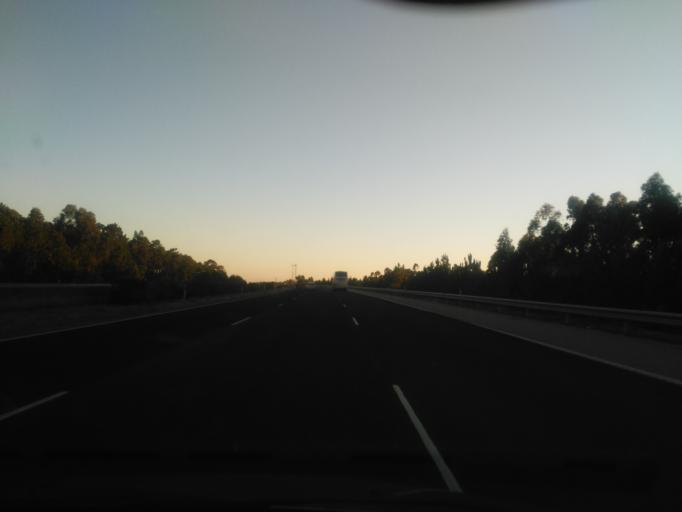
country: PT
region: Leiria
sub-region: Leiria
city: Maceira
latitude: 39.6931
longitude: -8.9299
